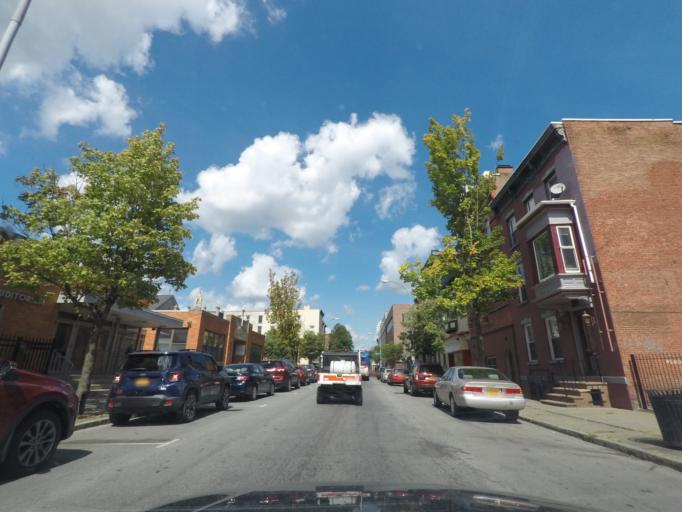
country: US
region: New York
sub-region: Rensselaer County
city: Troy
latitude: 42.7292
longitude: -73.6895
